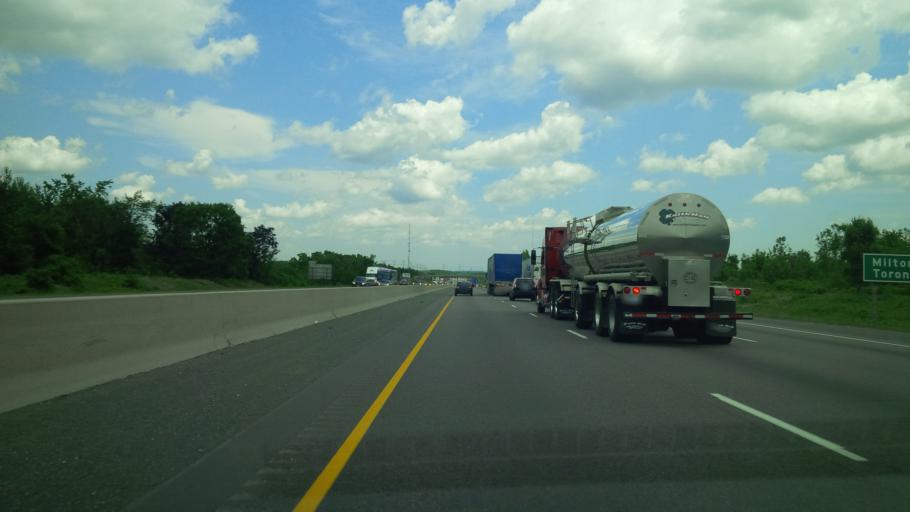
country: CA
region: Ontario
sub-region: Wellington County
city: Guelph
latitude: 43.4583
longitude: -80.1102
